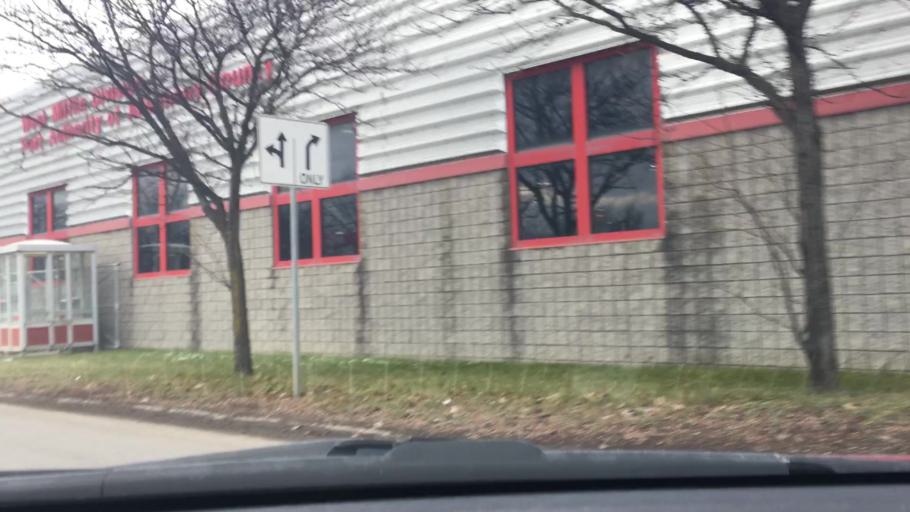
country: US
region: Pennsylvania
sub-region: Allegheny County
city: West Homestead
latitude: 40.3619
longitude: -79.9315
